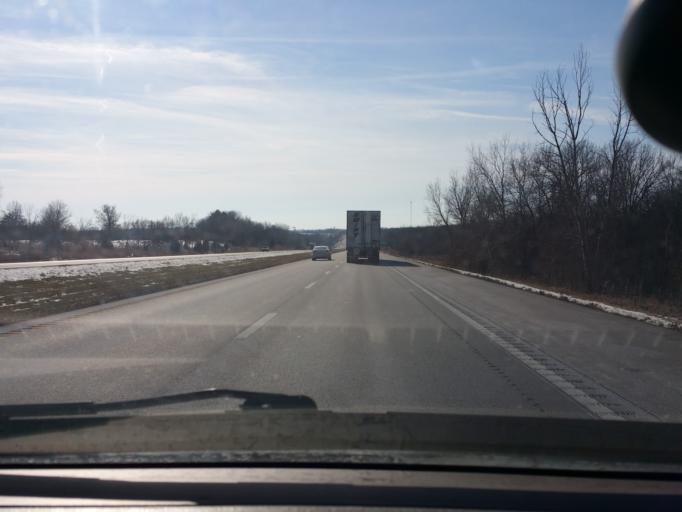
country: US
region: Missouri
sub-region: Clinton County
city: Cameron
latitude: 39.7797
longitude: -94.2097
